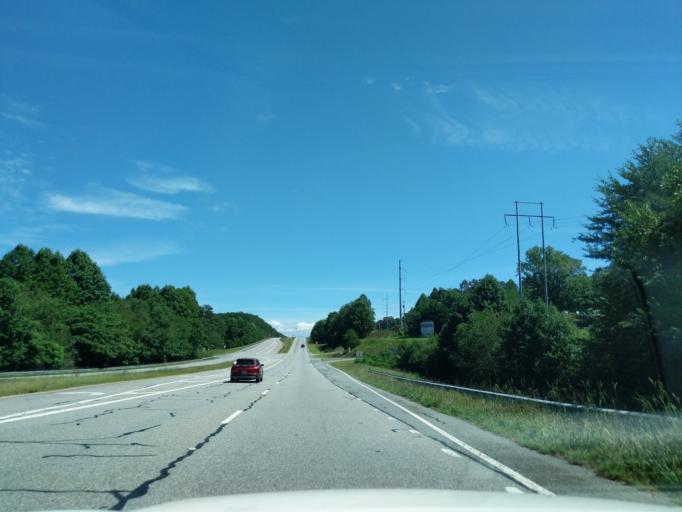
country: US
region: Georgia
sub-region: Fannin County
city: Blue Ridge
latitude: 34.8930
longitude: -84.2500
